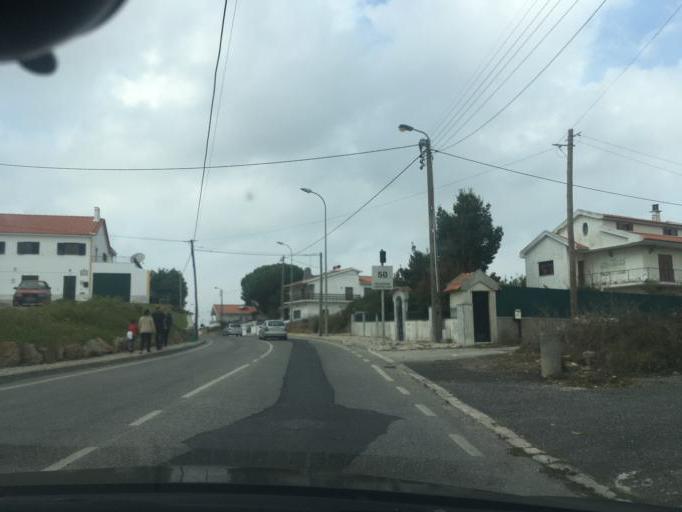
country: PT
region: Lisbon
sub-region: Sintra
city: Sintra
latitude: 38.8371
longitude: -9.3668
